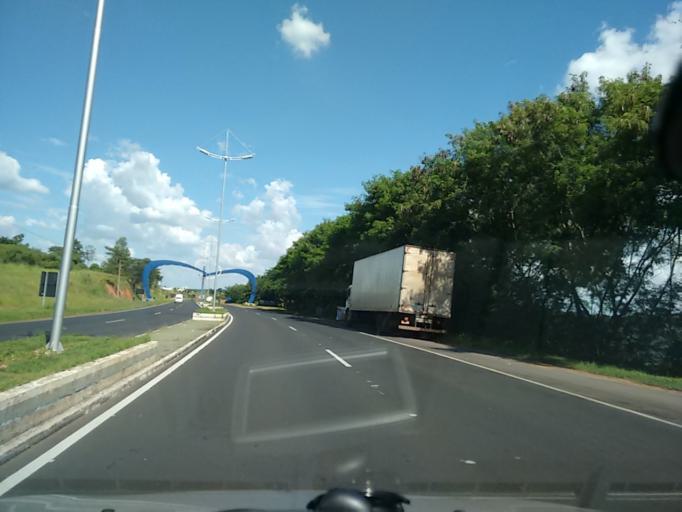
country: BR
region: Sao Paulo
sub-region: Pompeia
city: Pompeia
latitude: -22.1172
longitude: -50.1561
